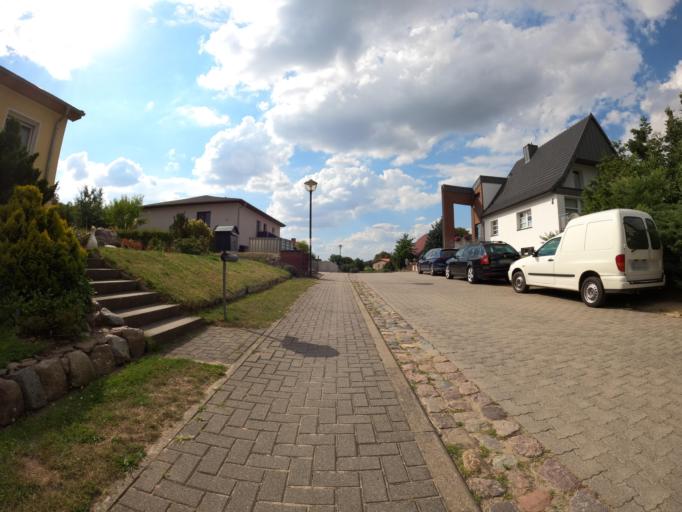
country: DE
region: Mecklenburg-Vorpommern
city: Woldegk
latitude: 53.3912
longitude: 13.5930
